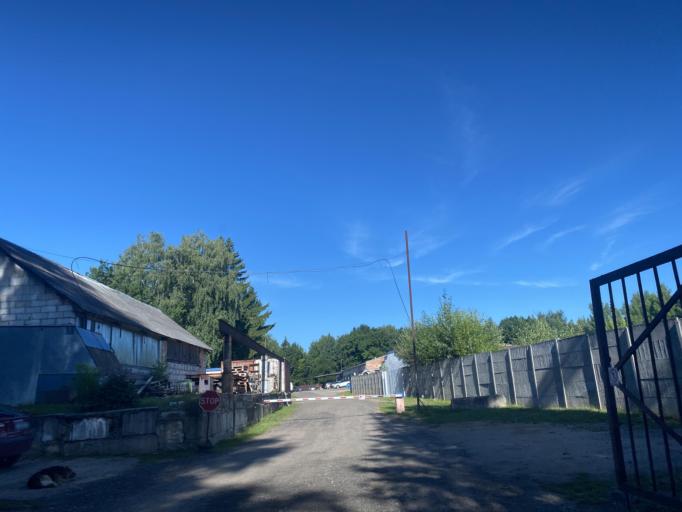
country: BY
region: Minsk
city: Zhdanovichy
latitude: 53.9123
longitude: 27.3748
